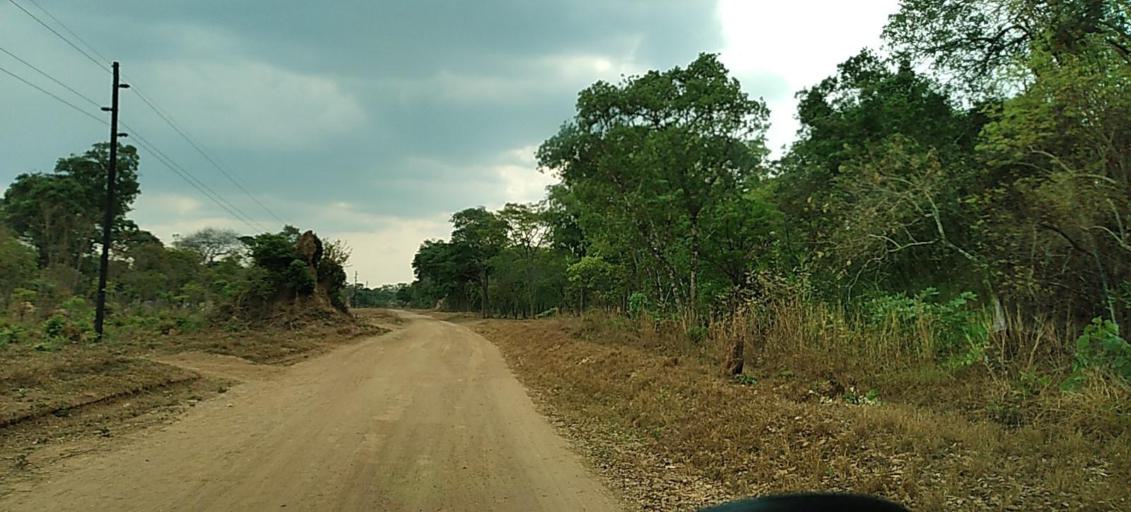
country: ZM
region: North-Western
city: Solwezi
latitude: -12.7799
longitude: 26.4791
